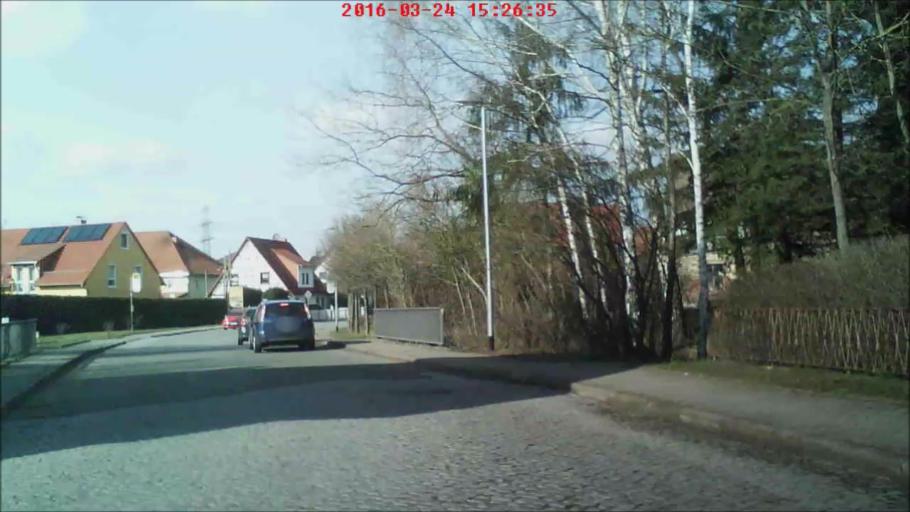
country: DE
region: Thuringia
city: Elxleben
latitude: 50.8676
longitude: 11.0541
